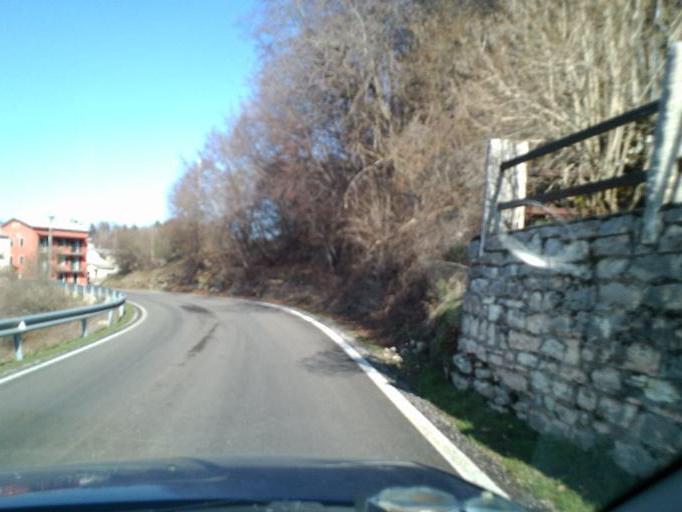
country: IT
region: Veneto
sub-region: Provincia di Verona
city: Bosco Chiesanuova
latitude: 45.6305
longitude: 11.0308
